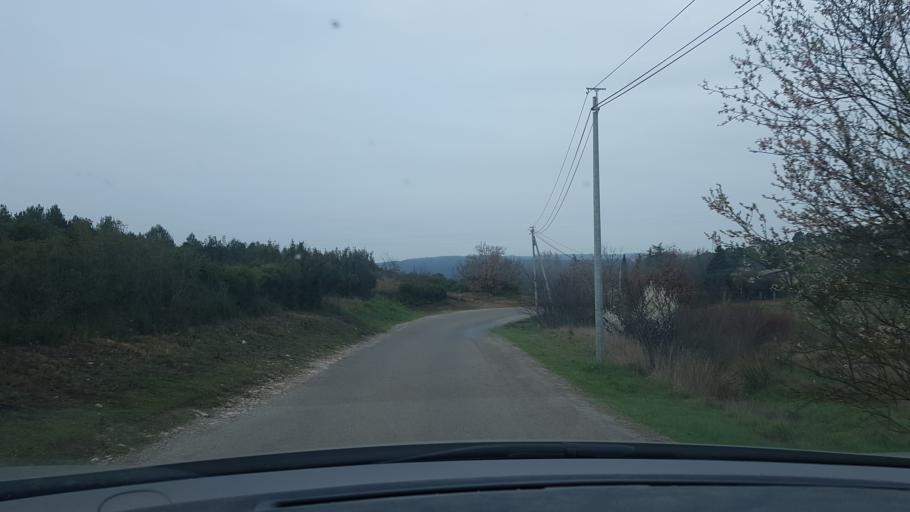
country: FR
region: Provence-Alpes-Cote d'Azur
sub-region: Departement des Bouches-du-Rhone
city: Gardanne
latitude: 43.4782
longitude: 5.4662
